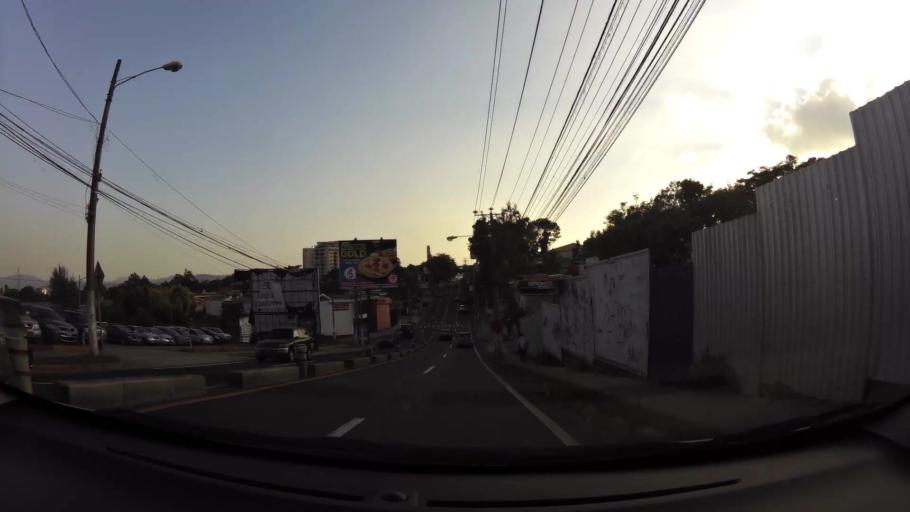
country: SV
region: La Libertad
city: Antiguo Cuscatlan
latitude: 13.7025
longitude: -89.2496
